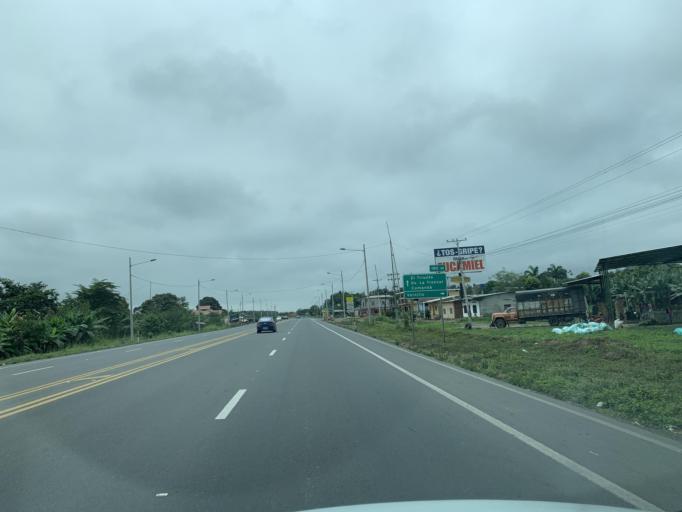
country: EC
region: Guayas
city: Coronel Marcelino Mariduena
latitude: -2.3154
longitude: -79.4707
